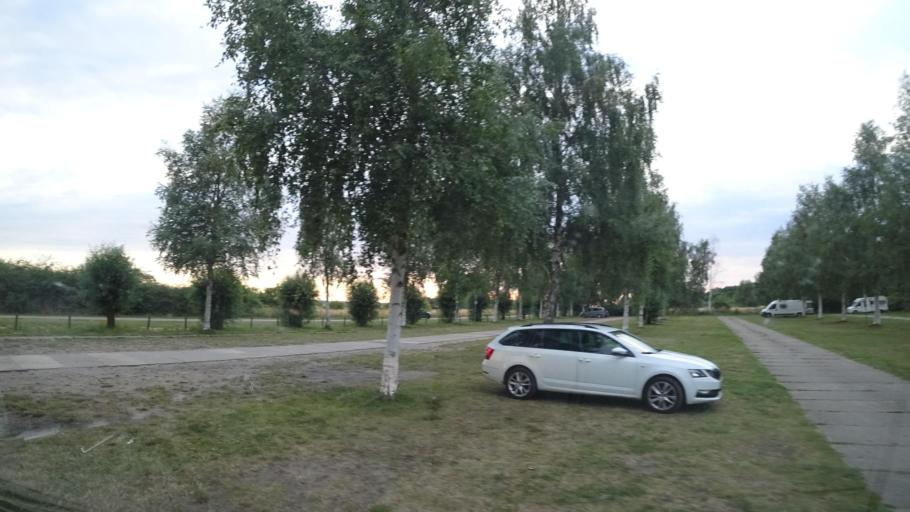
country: DE
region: Mecklenburg-Vorpommern
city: Kemnitz
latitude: 54.1128
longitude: 13.4831
